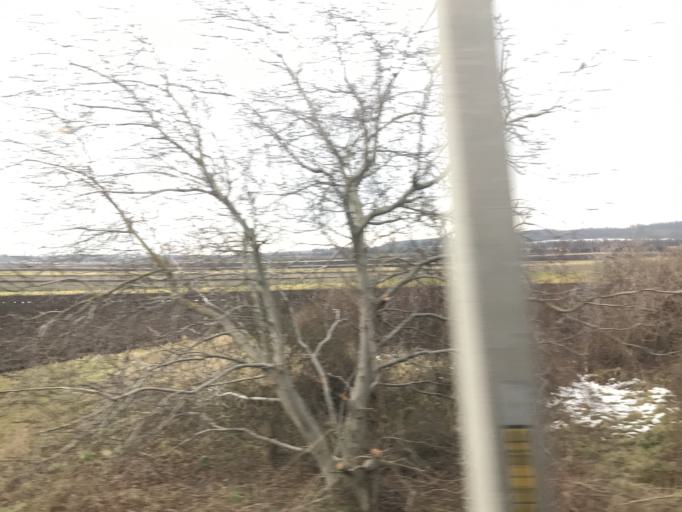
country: AT
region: Burgenland
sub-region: Politischer Bezirk Neusiedl am See
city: Parndorf
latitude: 47.9962
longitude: 16.8408
